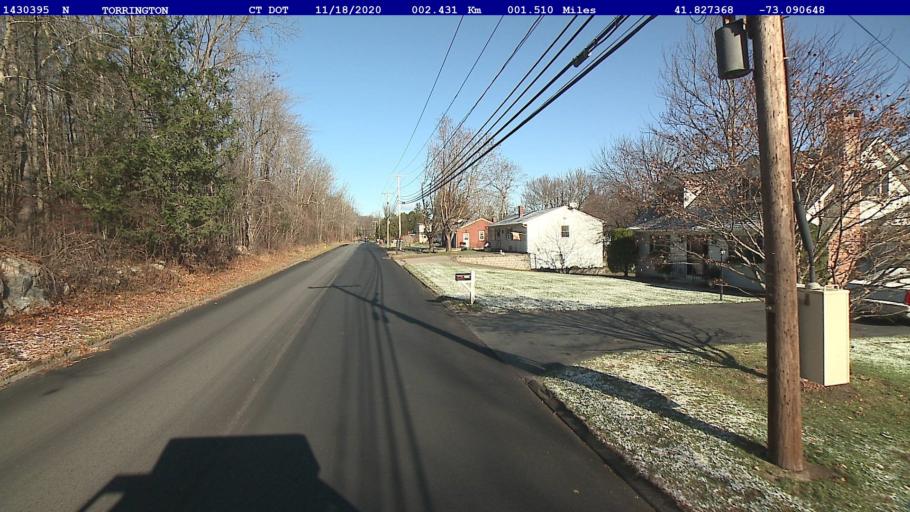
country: US
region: Connecticut
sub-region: Litchfield County
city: Torrington
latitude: 41.8274
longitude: -73.0906
